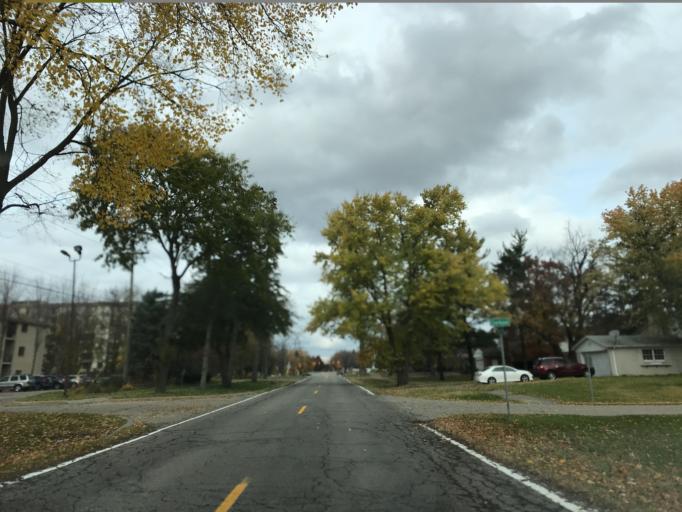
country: US
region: Michigan
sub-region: Oakland County
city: Bingham Farms
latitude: 42.4765
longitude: -83.2792
